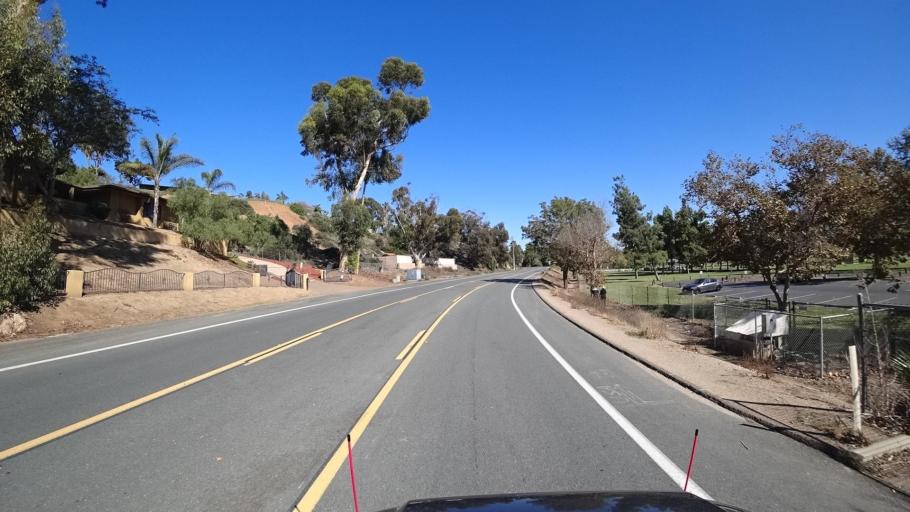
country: US
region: California
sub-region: San Diego County
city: Bonita
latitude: 32.6655
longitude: -117.0381
